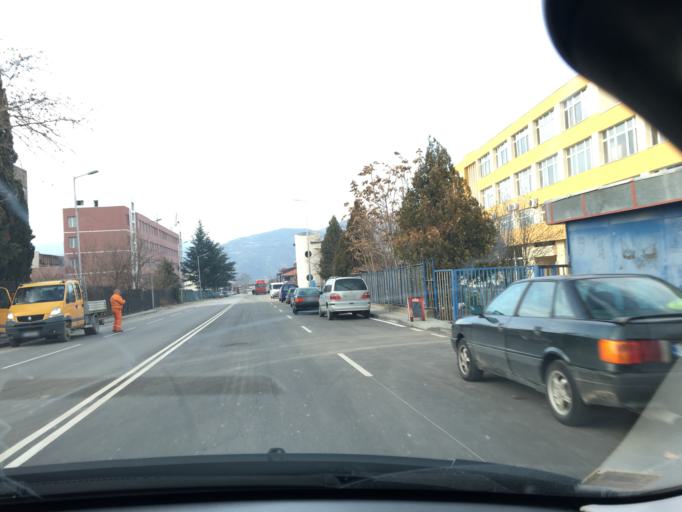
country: BG
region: Blagoevgrad
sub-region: Obshtina Sandanski
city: Sandanski
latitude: 41.5411
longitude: 23.2555
